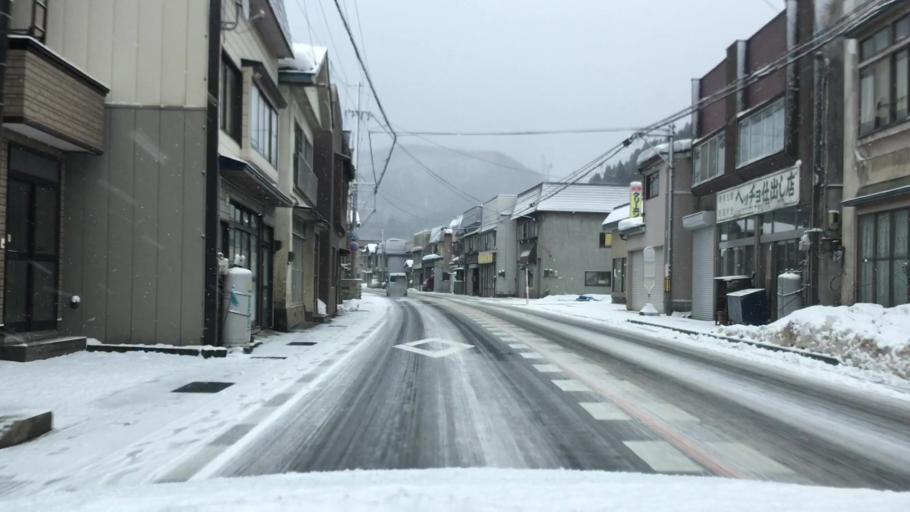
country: JP
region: Aomori
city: Kuroishi
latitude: 40.4741
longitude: 140.6268
